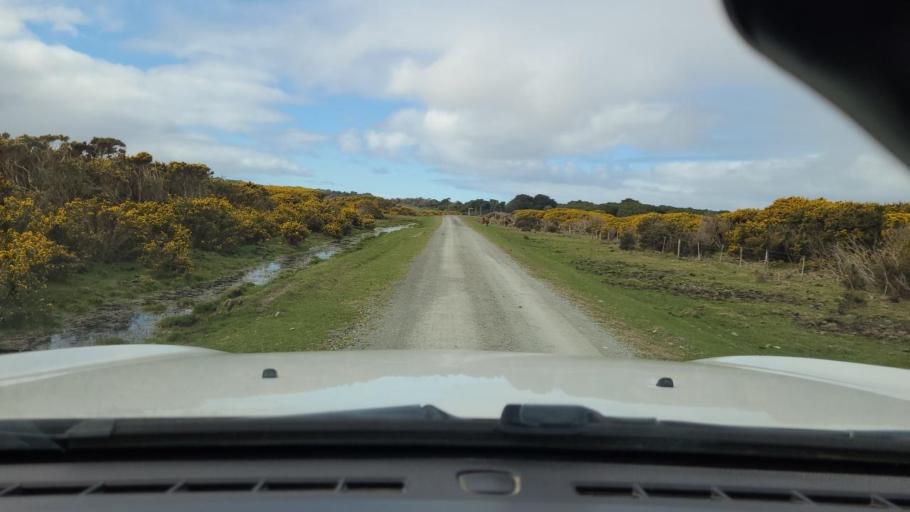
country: NZ
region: Chatham Islands
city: Waitangi
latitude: -43.9146
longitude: -176.4971
